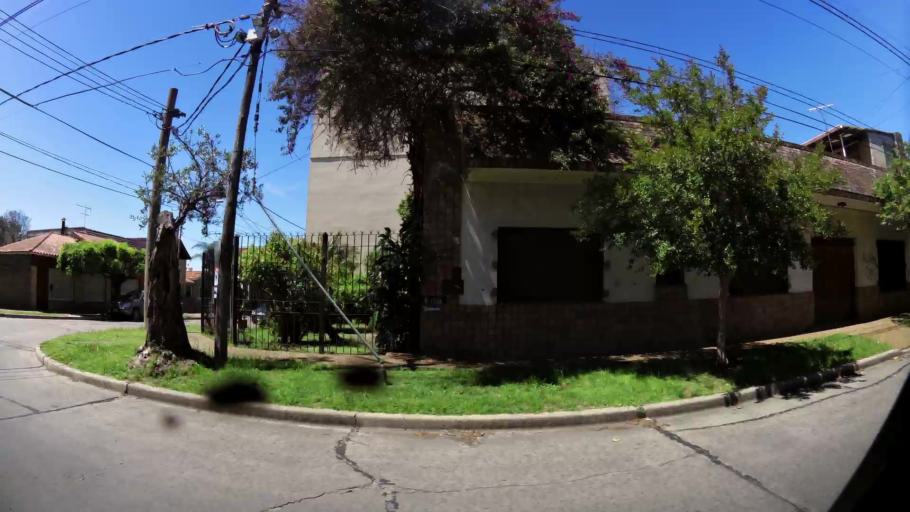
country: AR
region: Buenos Aires
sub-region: Partido de Quilmes
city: Quilmes
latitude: -34.7175
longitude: -58.2836
